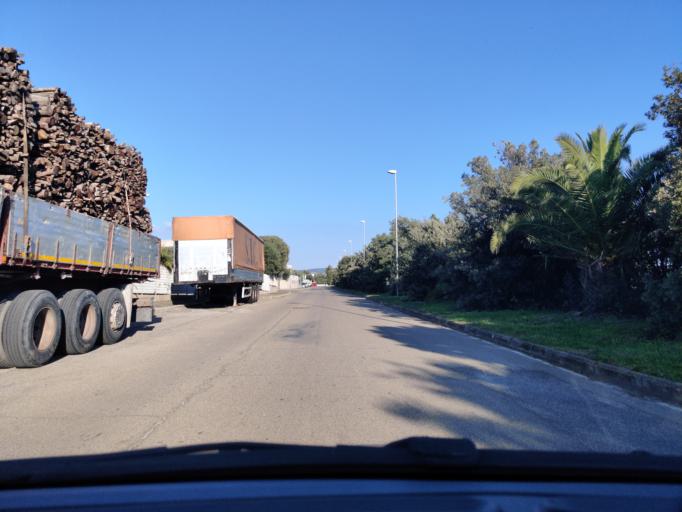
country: IT
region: Latium
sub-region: Citta metropolitana di Roma Capitale
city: Aurelia
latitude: 42.1168
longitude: 11.7802
